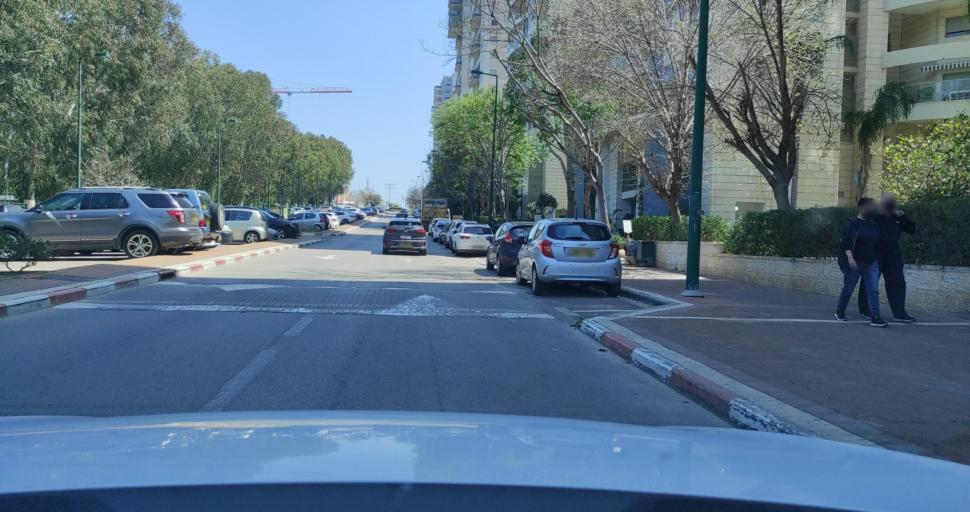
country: IL
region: Central District
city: Nordiyya
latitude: 32.3028
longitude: 34.8774
